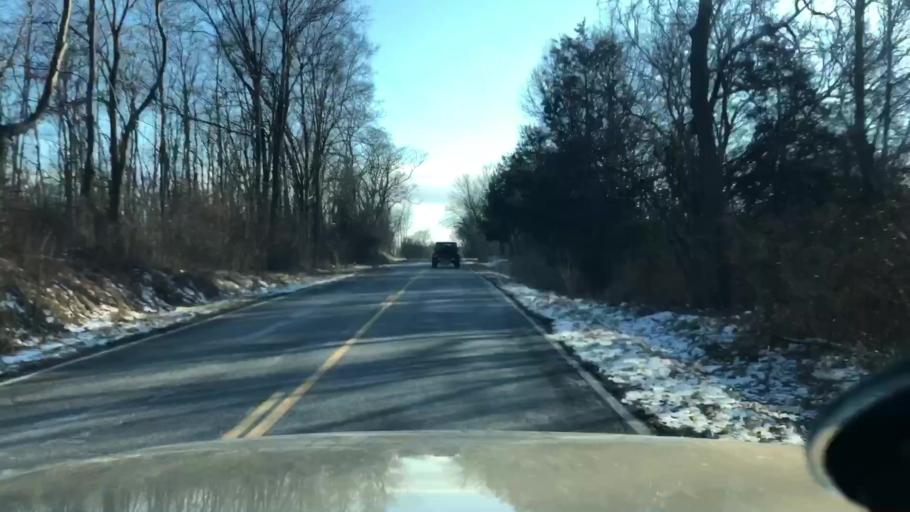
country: US
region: Michigan
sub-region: Jackson County
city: Vandercook Lake
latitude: 42.1276
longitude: -84.4515
